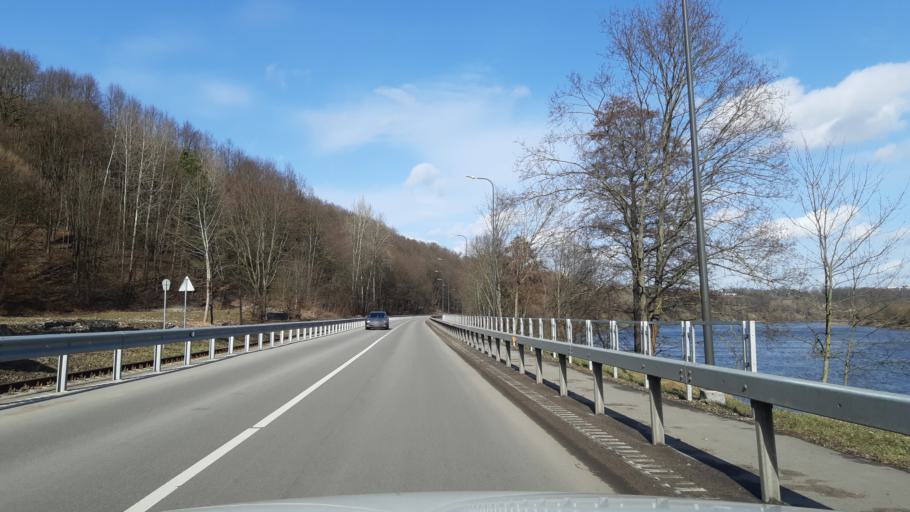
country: LT
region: Kauno apskritis
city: Dainava (Kaunas)
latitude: 54.8822
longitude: 23.9572
